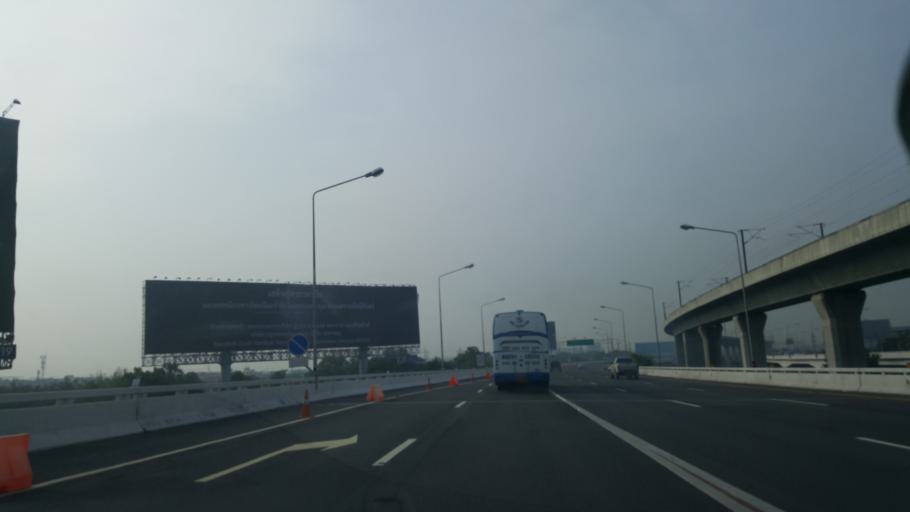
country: TH
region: Bangkok
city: Lat Krabang
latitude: 13.7260
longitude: 100.7605
